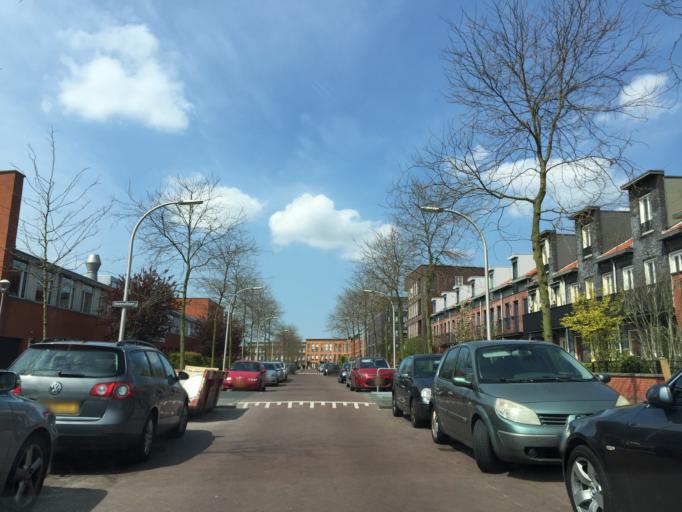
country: NL
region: South Holland
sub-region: Gemeente Den Haag
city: Ypenburg
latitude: 52.0448
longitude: 4.3750
